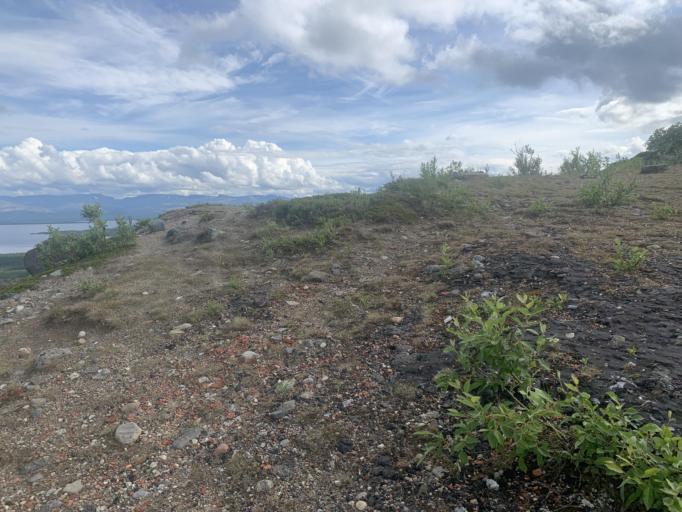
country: RU
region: Murmansk
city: Monchegorsk
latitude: 67.9167
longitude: 32.9785
